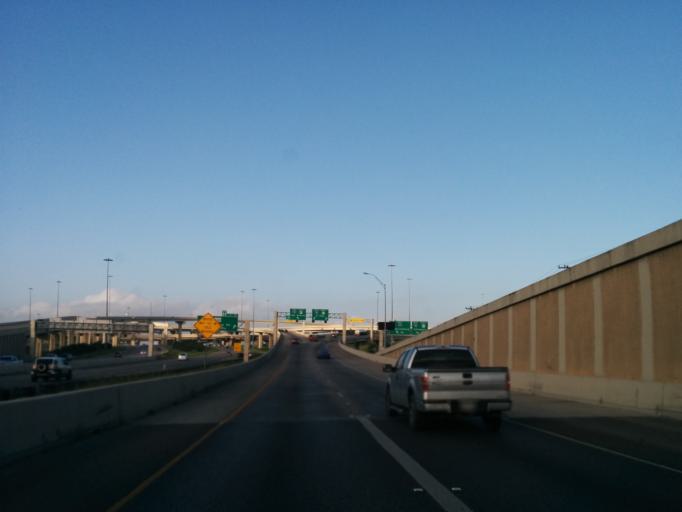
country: US
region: Texas
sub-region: Bexar County
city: Balcones Heights
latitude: 29.5069
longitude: -98.5448
